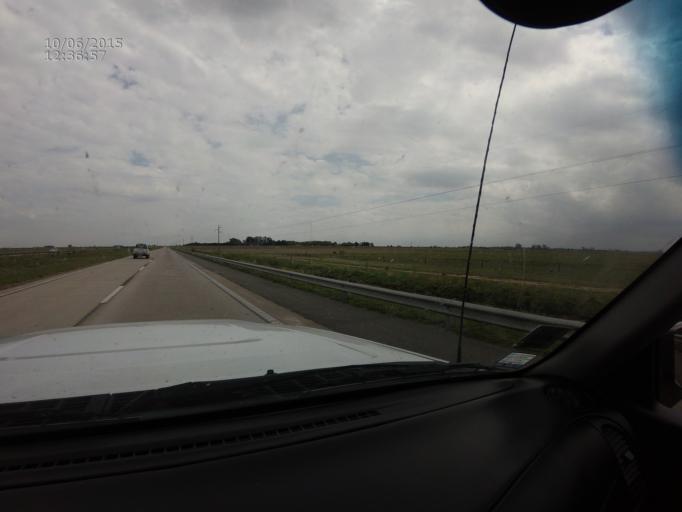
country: AR
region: Santa Fe
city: Carcarana
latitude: -32.8697
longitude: -61.2093
